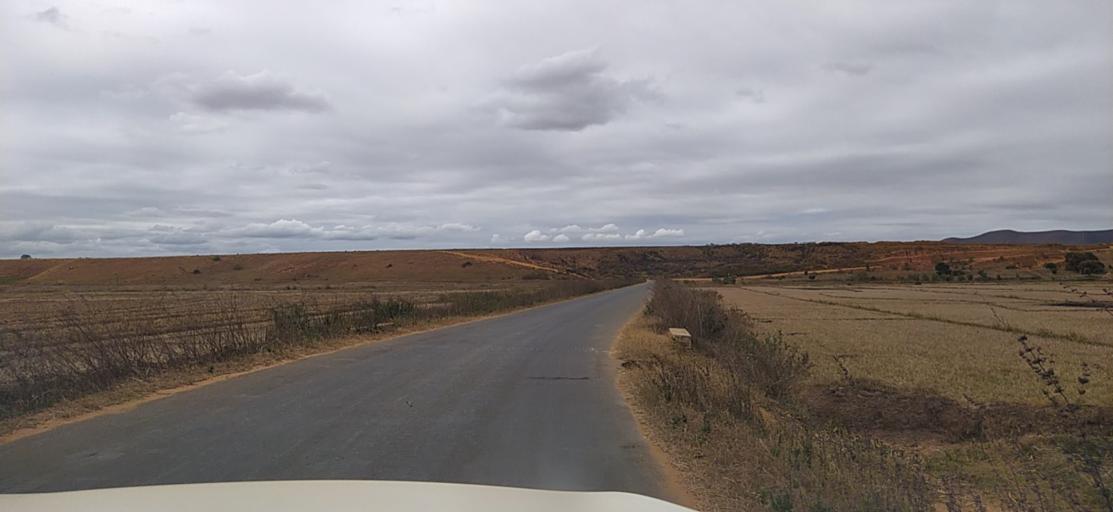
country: MG
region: Alaotra Mangoro
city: Ambatondrazaka
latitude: -17.9149
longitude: 48.2589
